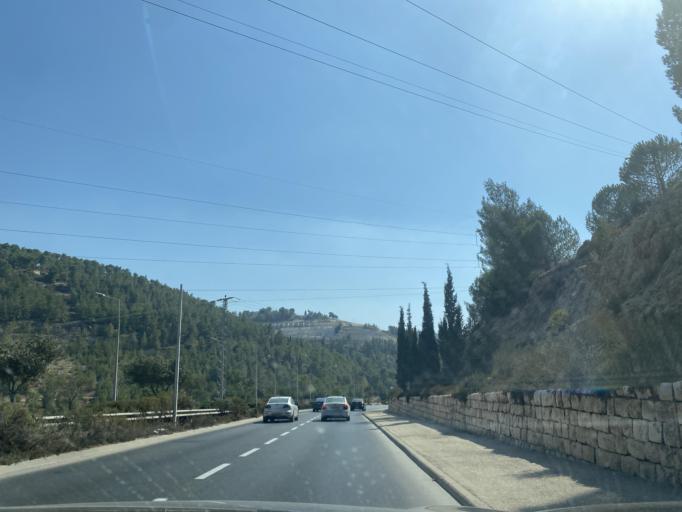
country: PS
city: Khallat Hamamah
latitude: 31.7466
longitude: 35.1812
